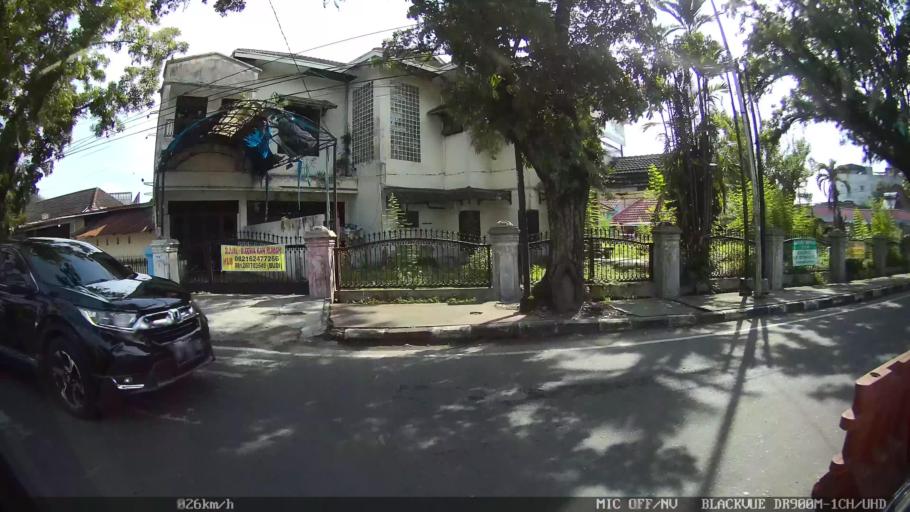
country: ID
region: North Sumatra
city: Medan
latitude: 3.5723
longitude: 98.6599
